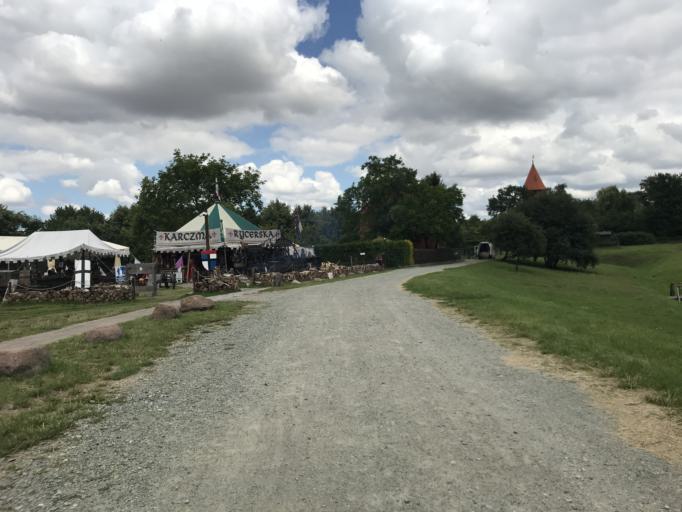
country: PL
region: Pomeranian Voivodeship
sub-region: Powiat malborski
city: Malbork
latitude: 54.0414
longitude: 19.0290
